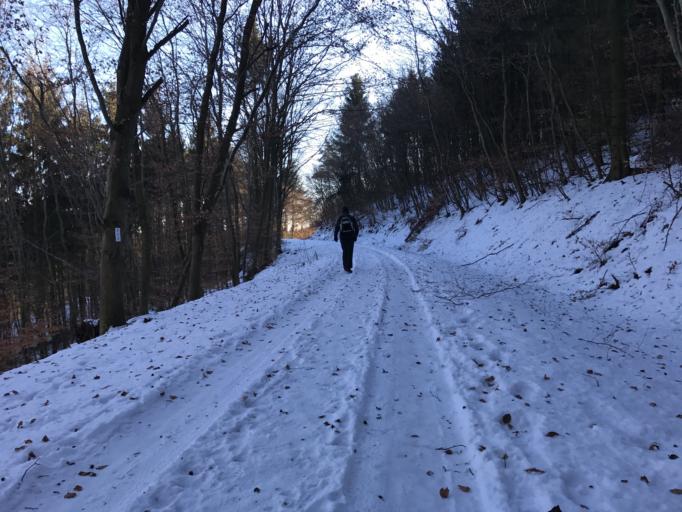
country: DE
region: Hesse
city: Eppstein
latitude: 50.1268
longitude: 8.3924
